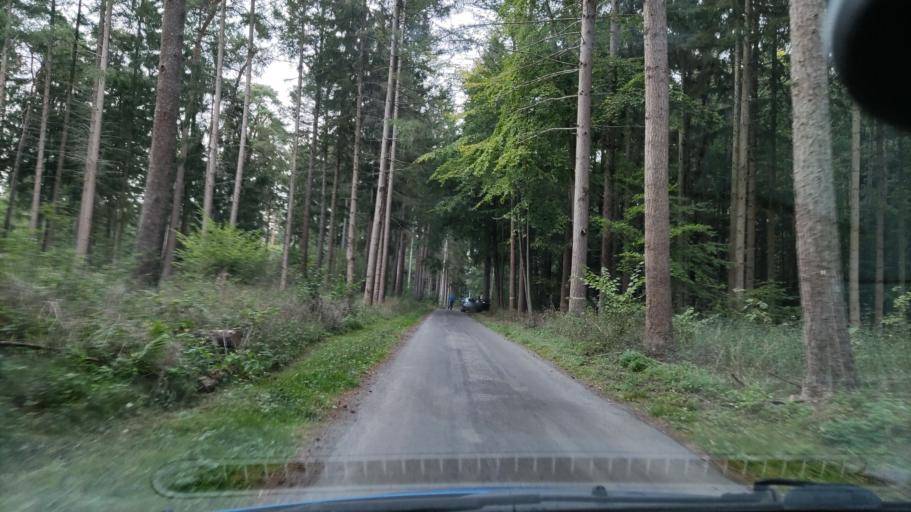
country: DE
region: Lower Saxony
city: Karwitz
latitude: 53.0819
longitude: 10.9739
